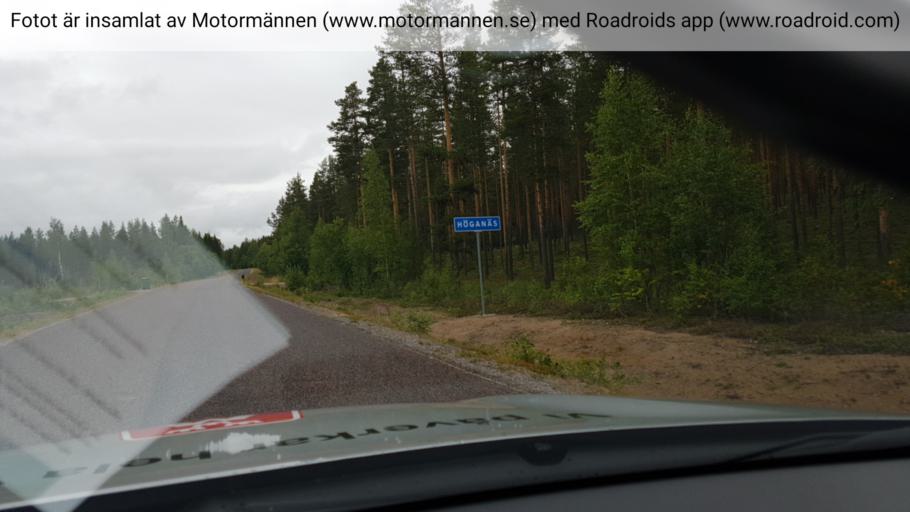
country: SE
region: Norrbotten
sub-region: Gallivare Kommun
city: Gaellivare
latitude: 66.5075
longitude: 20.5658
